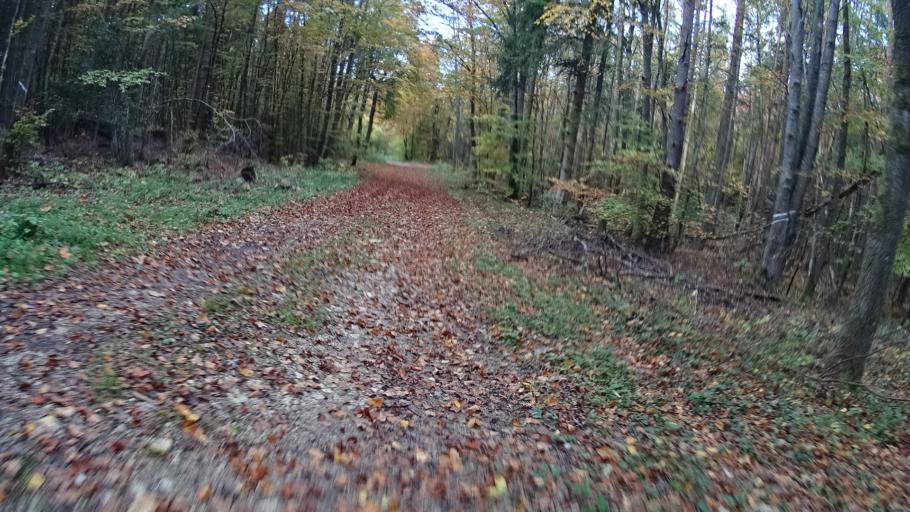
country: DE
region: Bavaria
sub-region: Upper Bavaria
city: Adelschlag
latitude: 48.8656
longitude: 11.2279
